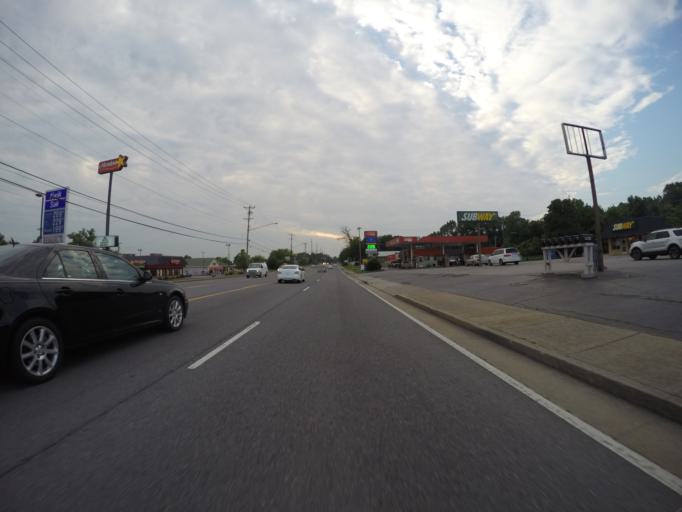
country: US
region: Tennessee
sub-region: Davidson County
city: Lakewood
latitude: 36.2561
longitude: -86.6542
